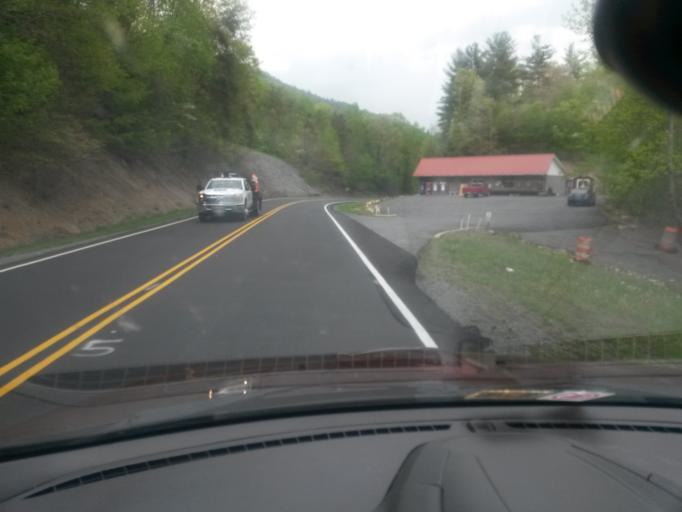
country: US
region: Virginia
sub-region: City of Covington
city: Covington
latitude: 37.8067
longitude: -80.0409
